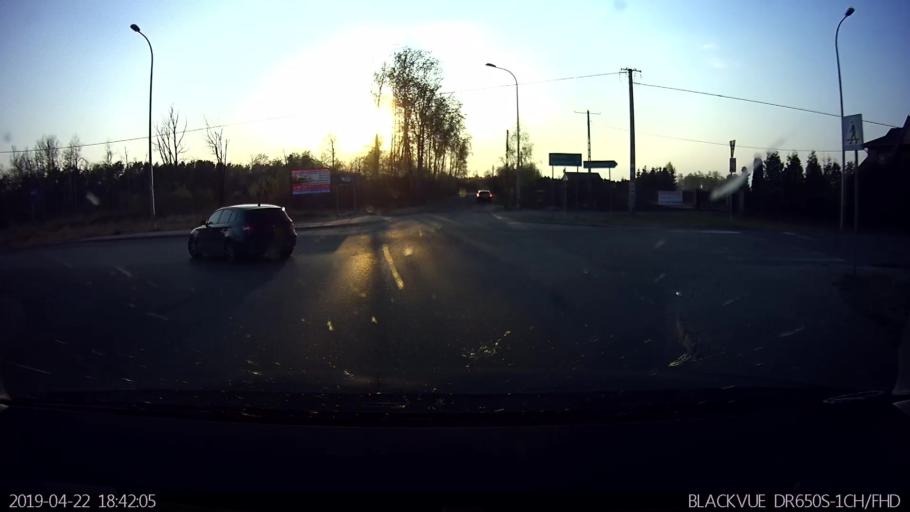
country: PL
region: Masovian Voivodeship
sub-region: Powiat wolominski
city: Dabrowka
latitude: 52.4492
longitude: 21.2599
